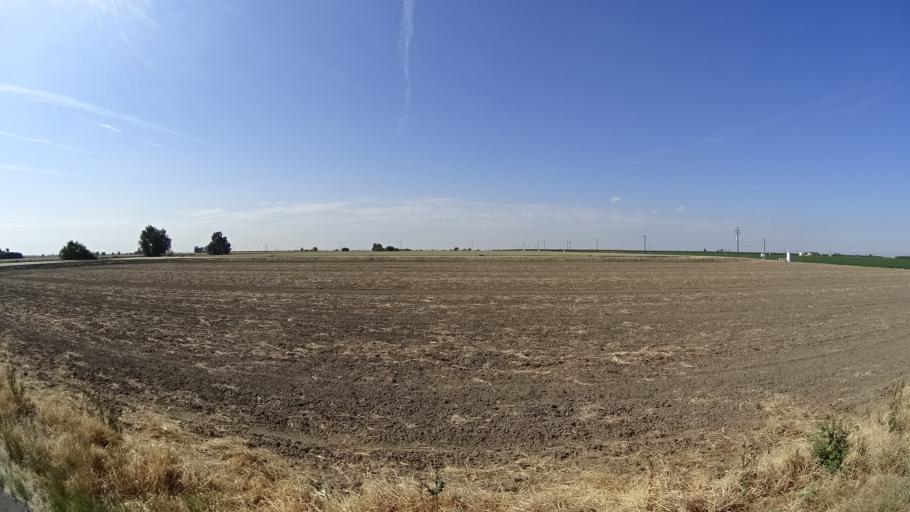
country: US
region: California
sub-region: Kings County
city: Home Garden
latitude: 36.2260
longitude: -119.5687
